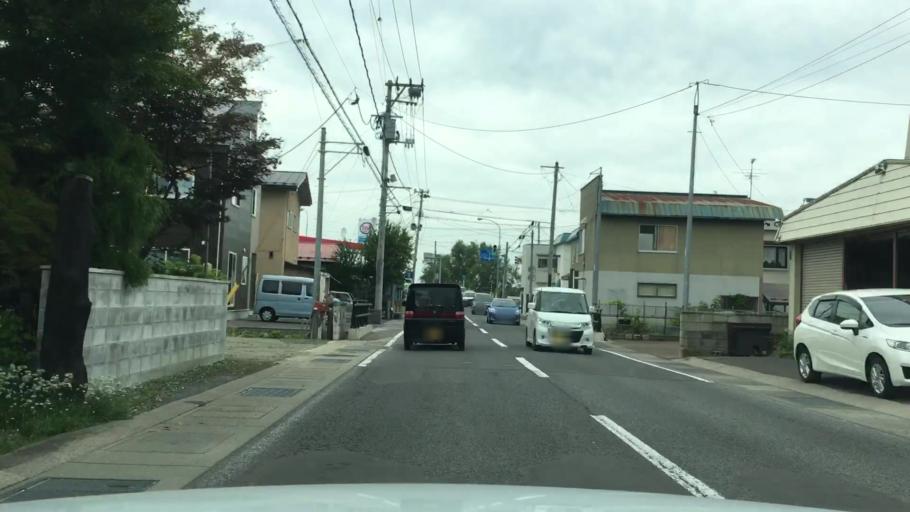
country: JP
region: Aomori
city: Hirosaki
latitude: 40.6137
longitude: 140.4620
